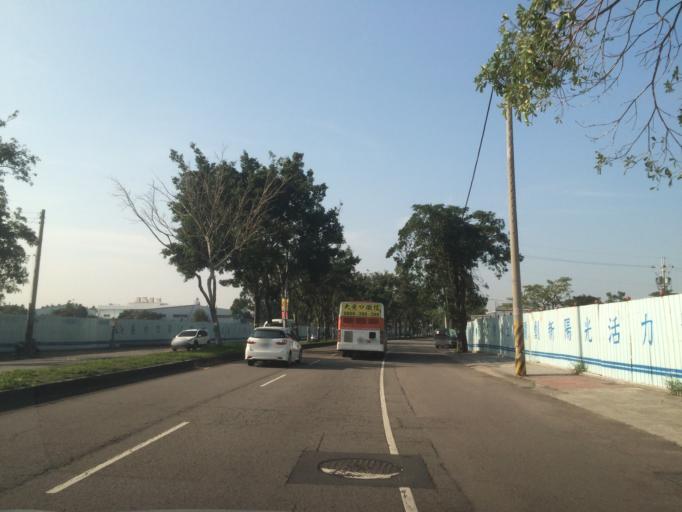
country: TW
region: Taiwan
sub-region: Taichung City
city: Taichung
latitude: 24.1825
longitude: 120.6802
